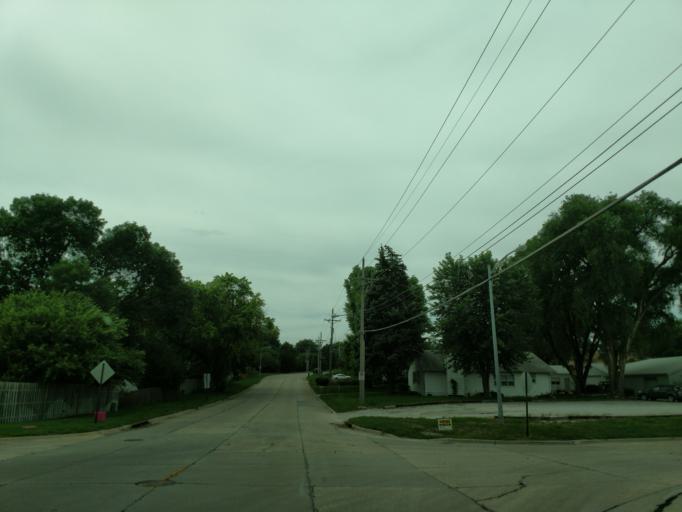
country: US
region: Nebraska
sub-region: Sarpy County
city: La Vista
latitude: 41.1933
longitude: -96.0334
